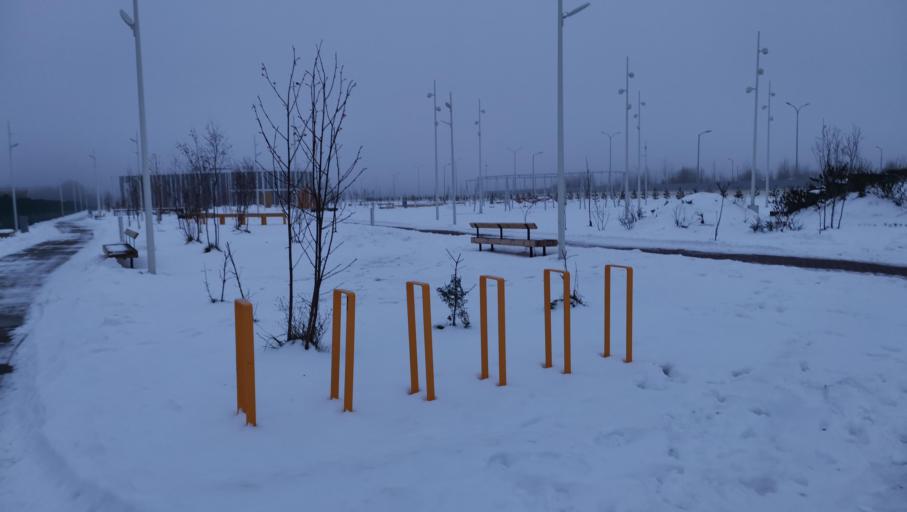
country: RU
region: Tatarstan
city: Sviyazhsk
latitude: 55.7456
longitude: 48.7459
